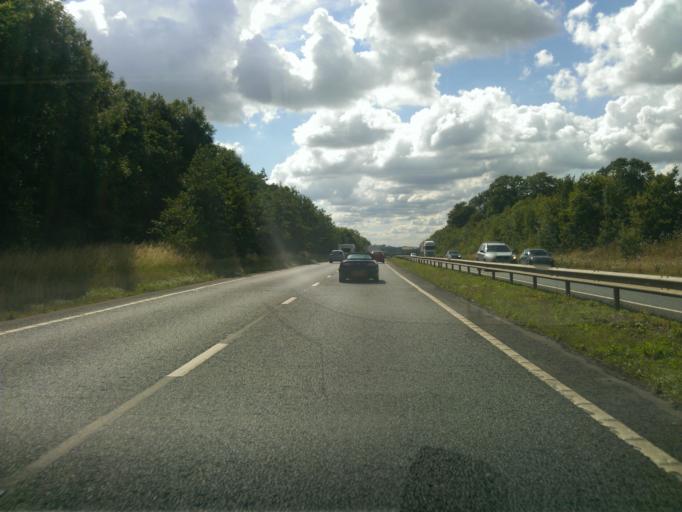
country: GB
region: England
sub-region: Leicestershire
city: Market Harborough
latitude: 52.4035
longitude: -0.9794
